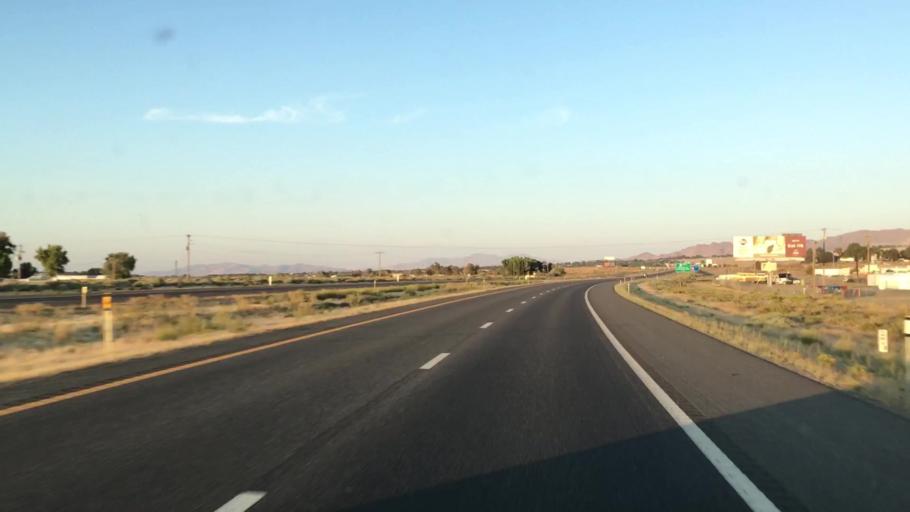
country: US
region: Nevada
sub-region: Humboldt County
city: Winnemucca
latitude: 40.9420
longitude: -117.7784
